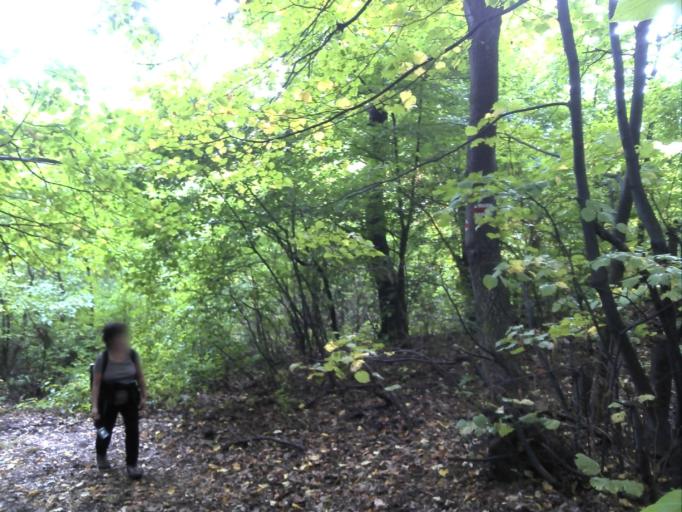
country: HU
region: Borsod-Abauj-Zemplen
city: Satoraljaujhely
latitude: 48.4057
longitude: 21.6388
